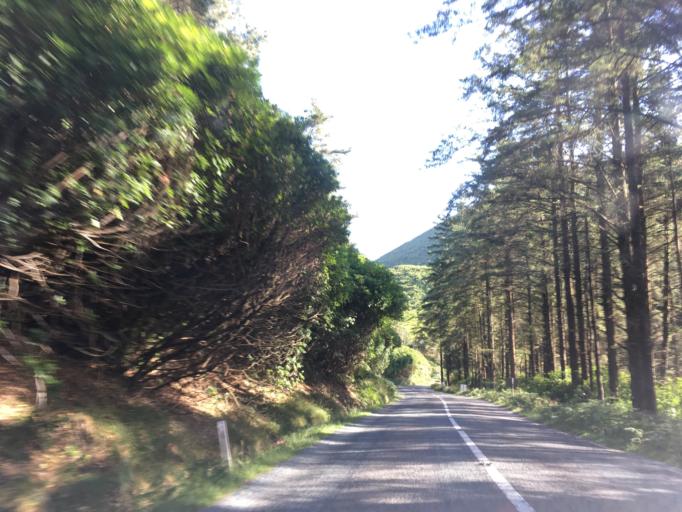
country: IE
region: Munster
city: Cahir
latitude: 52.2560
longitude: -7.9594
